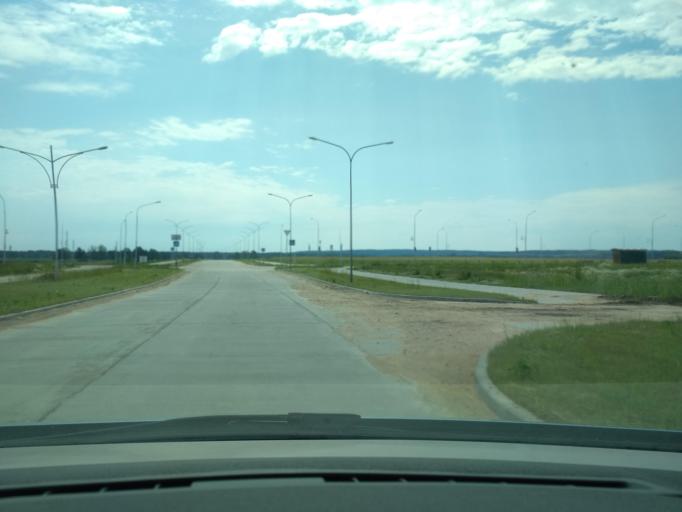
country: BY
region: Grodnenskaya
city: Astravyets
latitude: 54.5994
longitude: 25.9613
